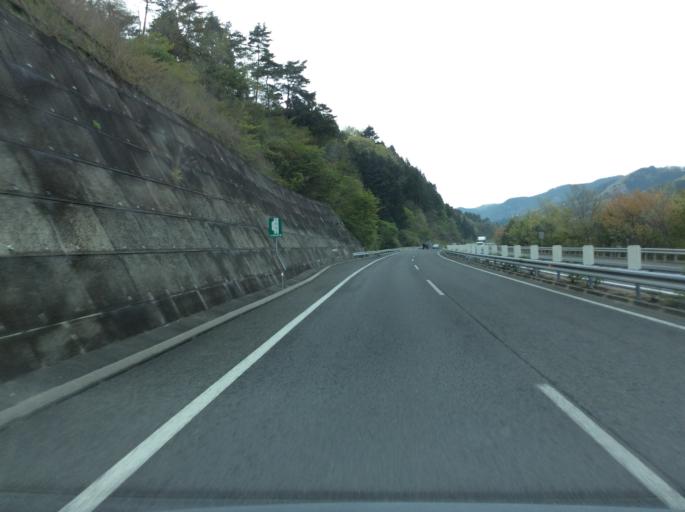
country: JP
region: Fukushima
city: Iwaki
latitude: 37.1105
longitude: 140.7559
